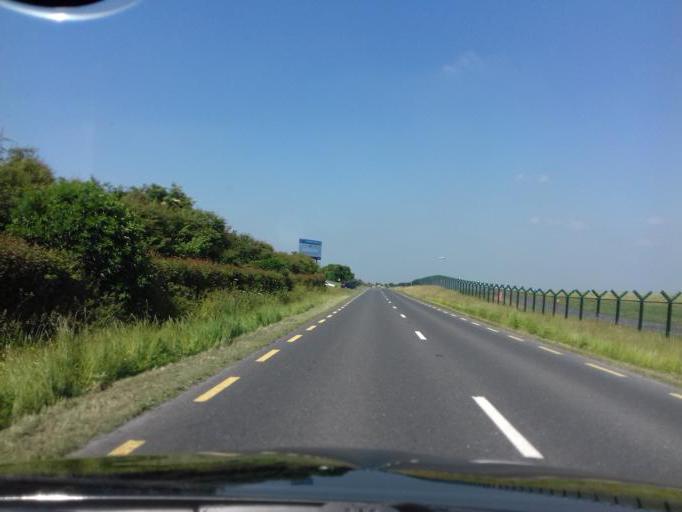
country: IE
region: Leinster
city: Ballymun
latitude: 53.4204
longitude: -6.2885
